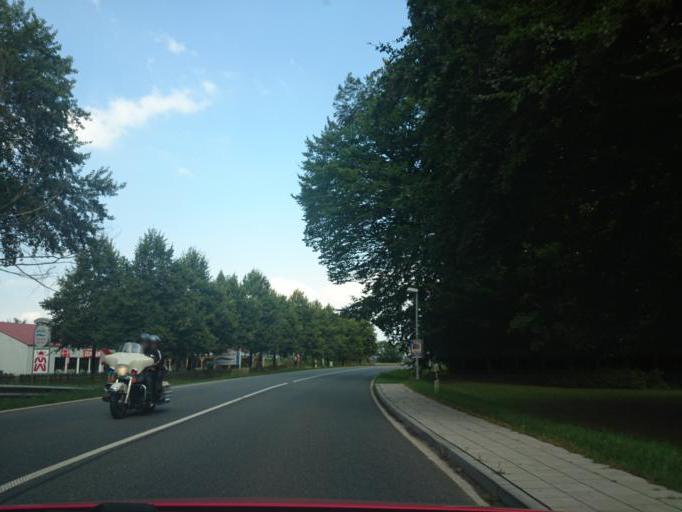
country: DE
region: Mecklenburg-Vorpommern
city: Velgast
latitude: 54.3030
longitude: 12.7997
